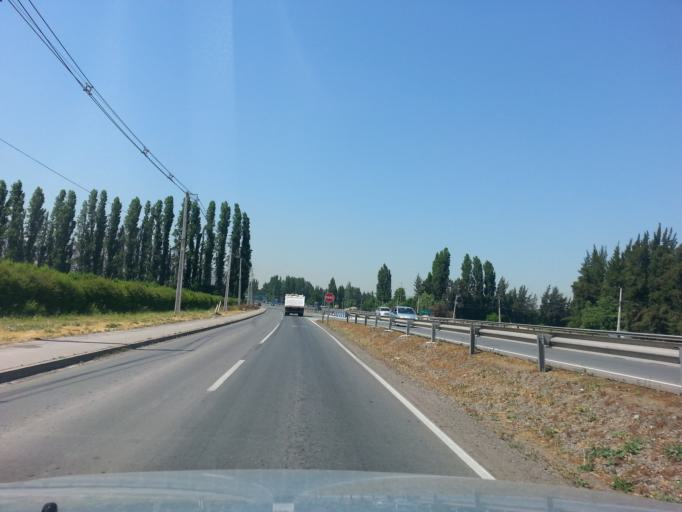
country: CL
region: Santiago Metropolitan
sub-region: Provincia de Chacabuco
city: Chicureo Abajo
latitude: -33.2786
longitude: -70.7025
